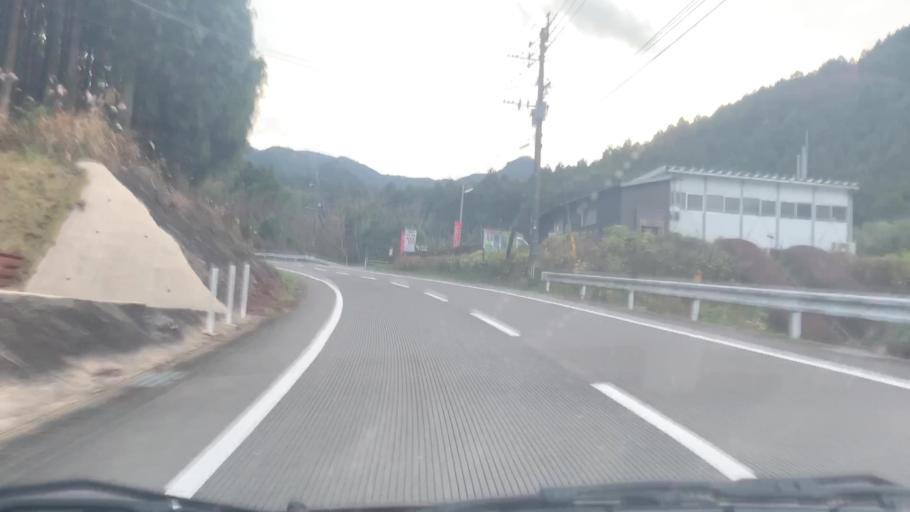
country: JP
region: Saga Prefecture
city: Kashima
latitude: 33.0029
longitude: 130.0631
